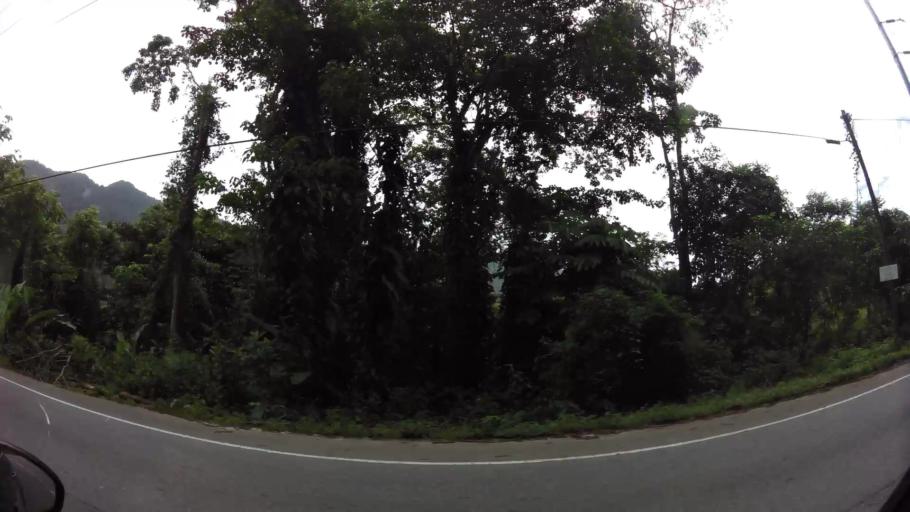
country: TT
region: Diego Martin
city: Petit Valley
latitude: 10.7590
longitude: -61.4451
